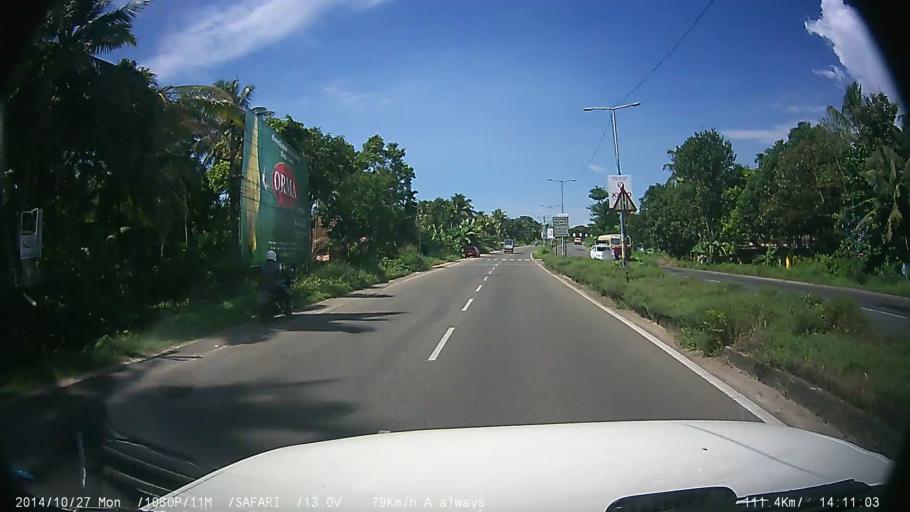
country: IN
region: Kerala
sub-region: Alappuzha
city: Kutiatodu
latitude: 9.7889
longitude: 76.3172
